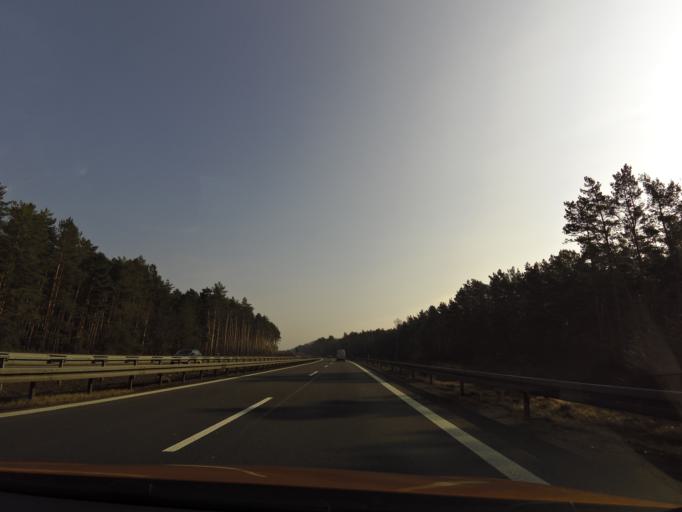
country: DE
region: Brandenburg
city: Storkow
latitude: 52.3138
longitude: 13.9183
